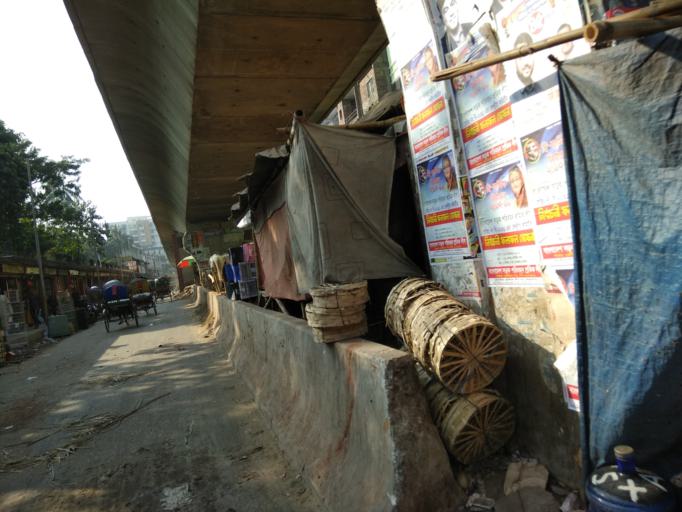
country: BD
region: Dhaka
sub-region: Dhaka
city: Dhaka
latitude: 23.7233
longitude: 90.4055
